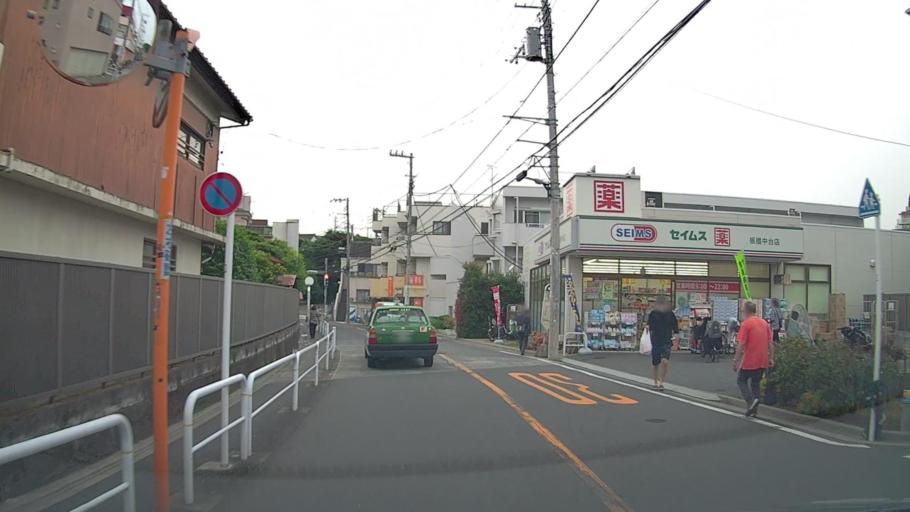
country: JP
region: Saitama
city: Shimotoda
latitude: 35.7666
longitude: 139.6777
